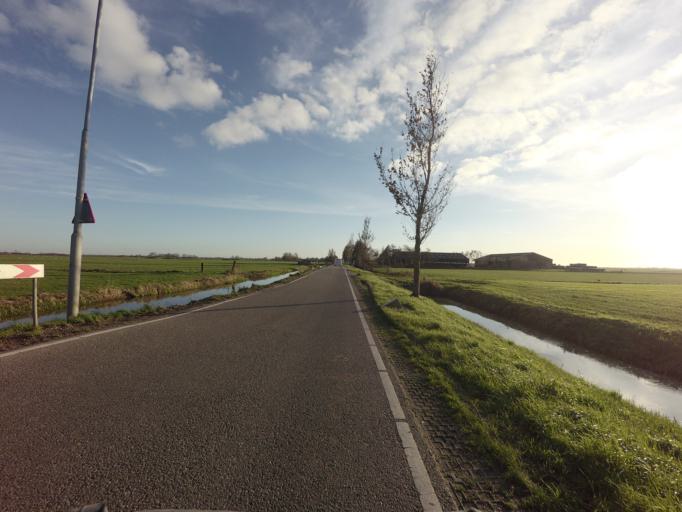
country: NL
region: South Holland
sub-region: Gemeente Nieuwkoop
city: Nieuwkoop
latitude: 52.1848
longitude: 4.8076
